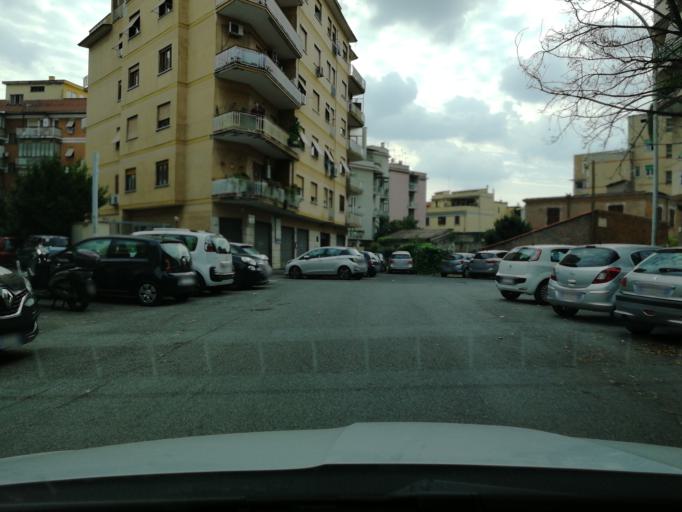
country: IT
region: Latium
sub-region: Citta metropolitana di Roma Capitale
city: Rome
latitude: 41.8607
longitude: 12.5496
